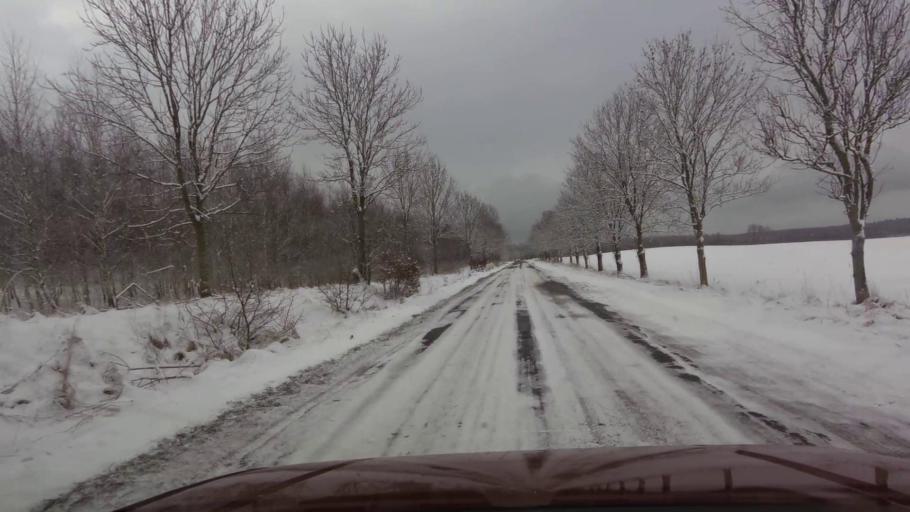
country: PL
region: West Pomeranian Voivodeship
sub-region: Powiat bialogardzki
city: Bialogard
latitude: 53.9397
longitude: 15.9586
